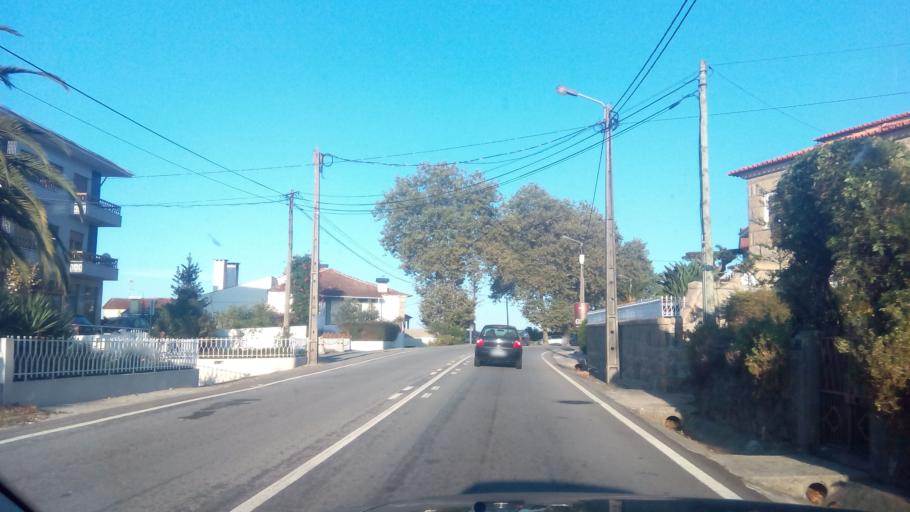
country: PT
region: Porto
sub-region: Paredes
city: Baltar
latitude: 41.1905
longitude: -8.3989
